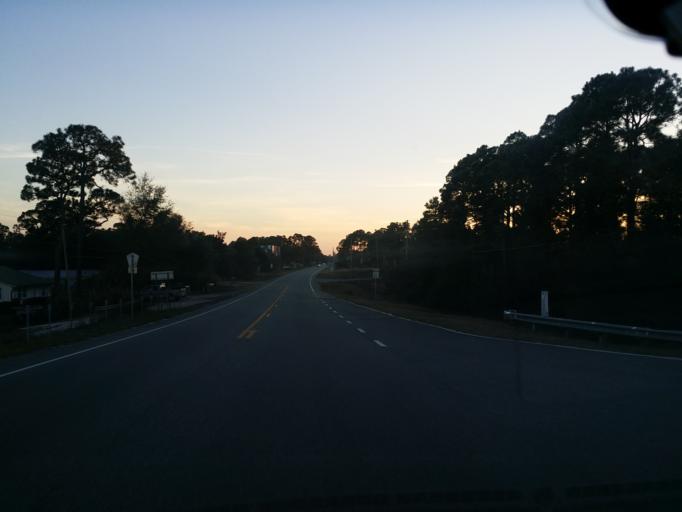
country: US
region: Florida
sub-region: Franklin County
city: Carrabelle
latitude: 29.8474
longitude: -84.6774
